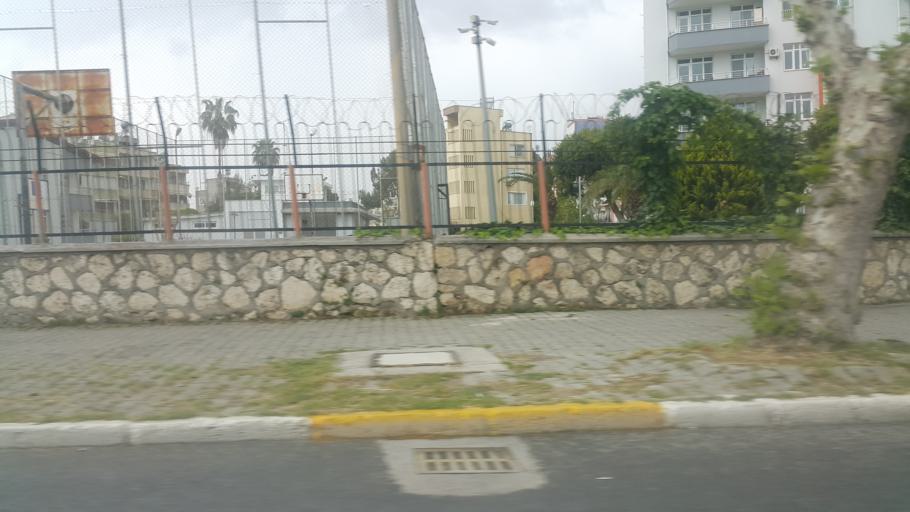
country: TR
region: Mersin
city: Mercin
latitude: 36.7780
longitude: 34.5864
